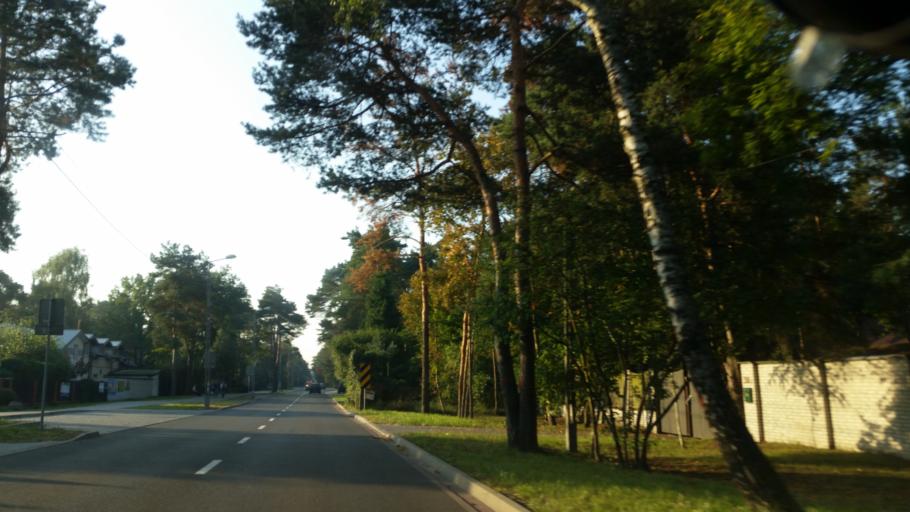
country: PL
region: Masovian Voivodeship
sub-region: Powiat otwocki
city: Jozefow
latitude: 52.1434
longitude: 21.2148
